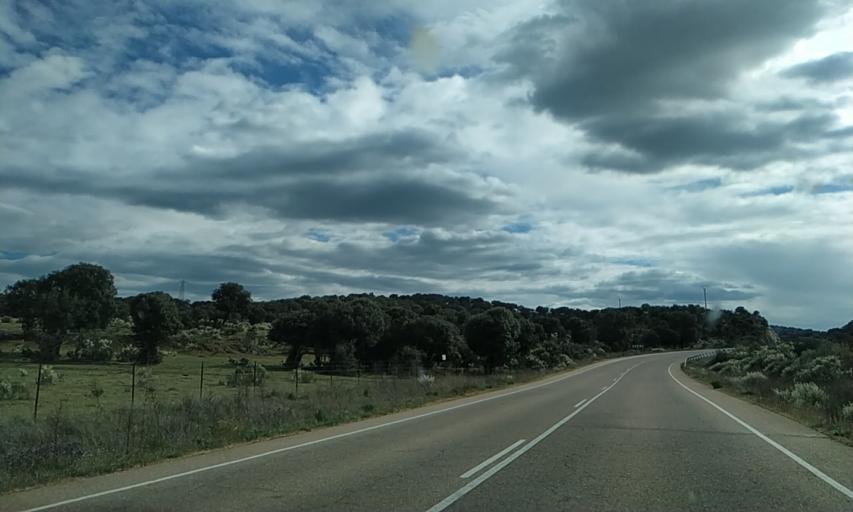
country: ES
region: Castille and Leon
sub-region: Provincia de Salamanca
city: Pastores
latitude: 40.5103
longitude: -6.5712
